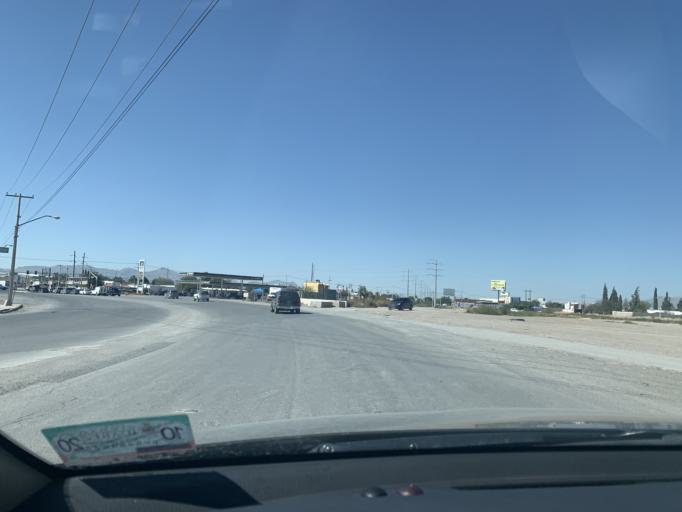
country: US
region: Texas
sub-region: El Paso County
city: Socorro
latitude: 31.6598
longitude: -106.3601
